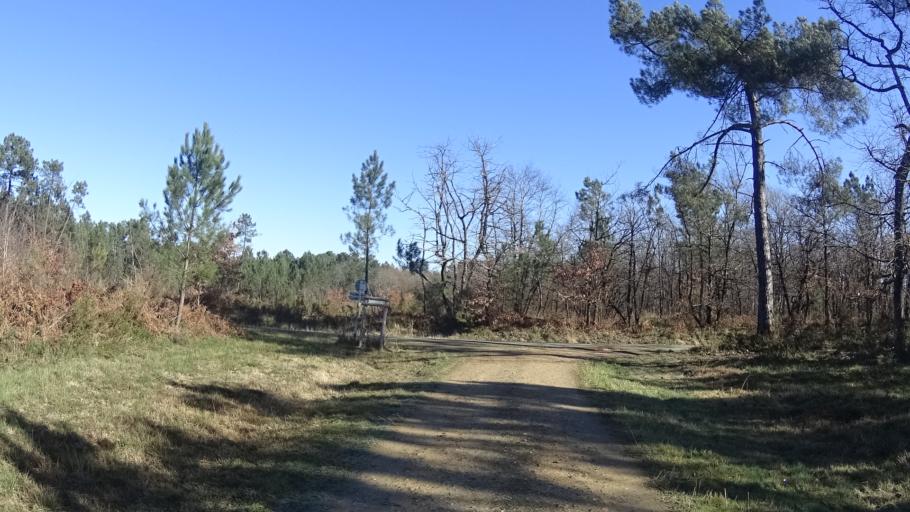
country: FR
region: Aquitaine
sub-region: Departement de la Dordogne
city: Saint-Aulaye
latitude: 45.2064
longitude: 0.0633
